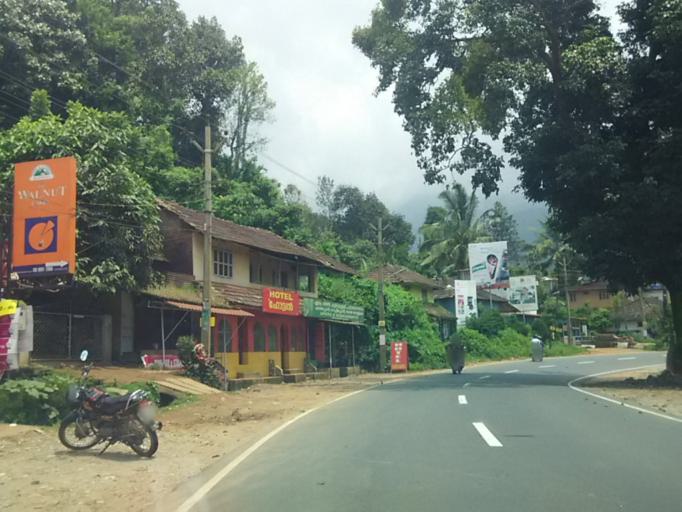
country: IN
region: Kerala
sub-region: Wayanad
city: Kalpetta
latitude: 11.5356
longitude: 76.0296
